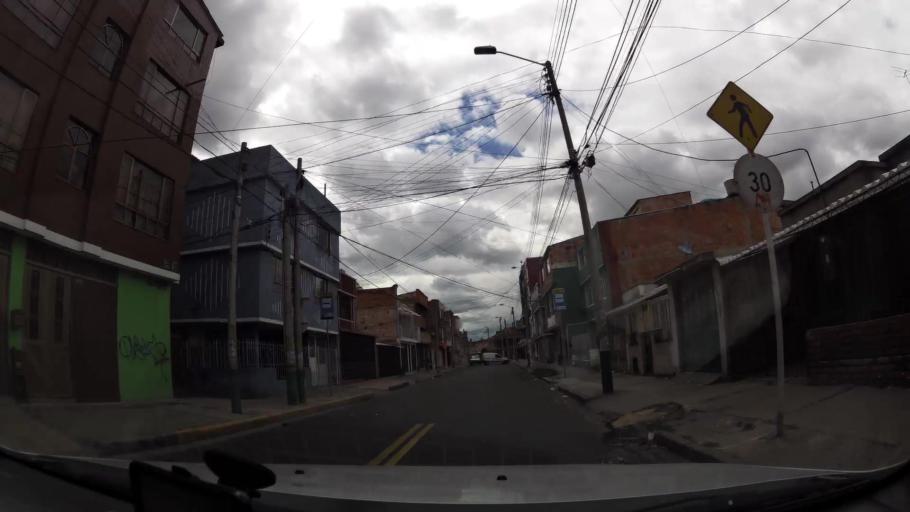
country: CO
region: Bogota D.C.
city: Bogota
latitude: 4.6046
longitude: -74.1291
